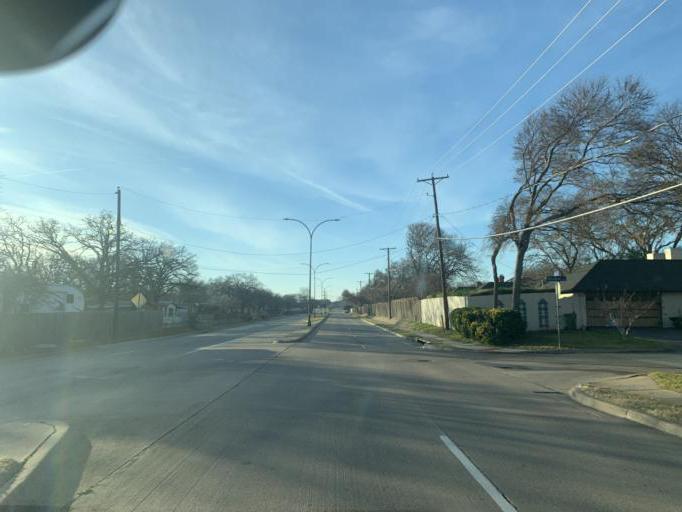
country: US
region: Texas
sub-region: Tarrant County
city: Arlington
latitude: 32.7709
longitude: -97.0737
